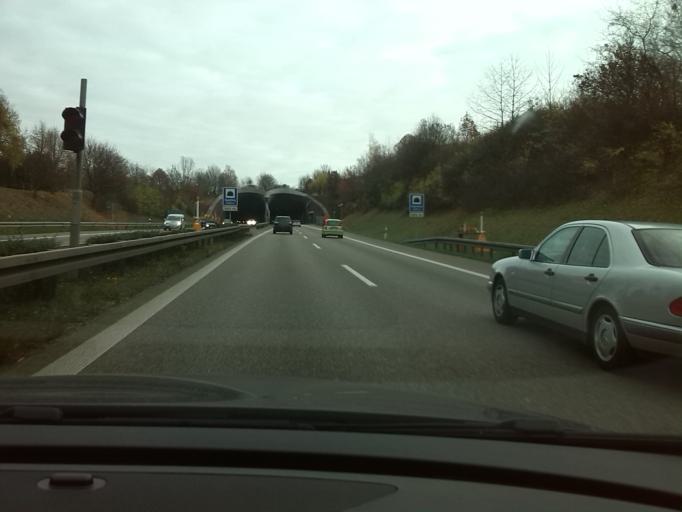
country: DE
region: Baden-Wuerttemberg
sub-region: Regierungsbezirk Stuttgart
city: Fellbach
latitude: 48.7988
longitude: 9.2645
